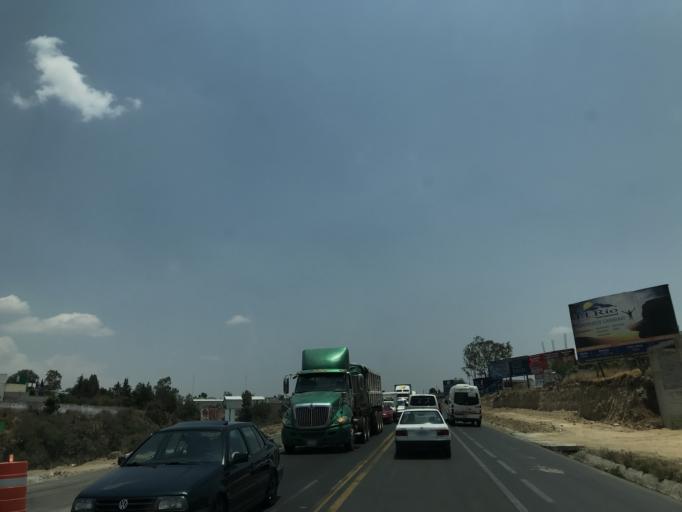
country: MX
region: Tlaxcala
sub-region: Apetatitlan de Antonio Carvajal
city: Belen Atzitzimititlan
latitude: 19.3474
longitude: -98.1948
